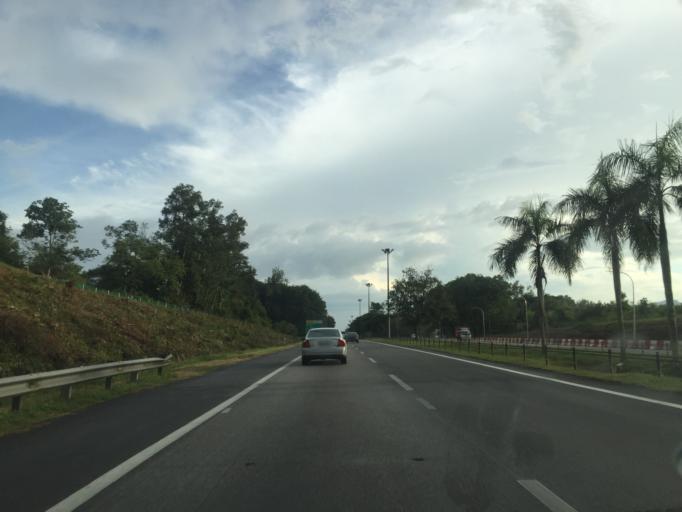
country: MY
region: Kedah
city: Gurun
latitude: 5.8394
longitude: 100.4868
